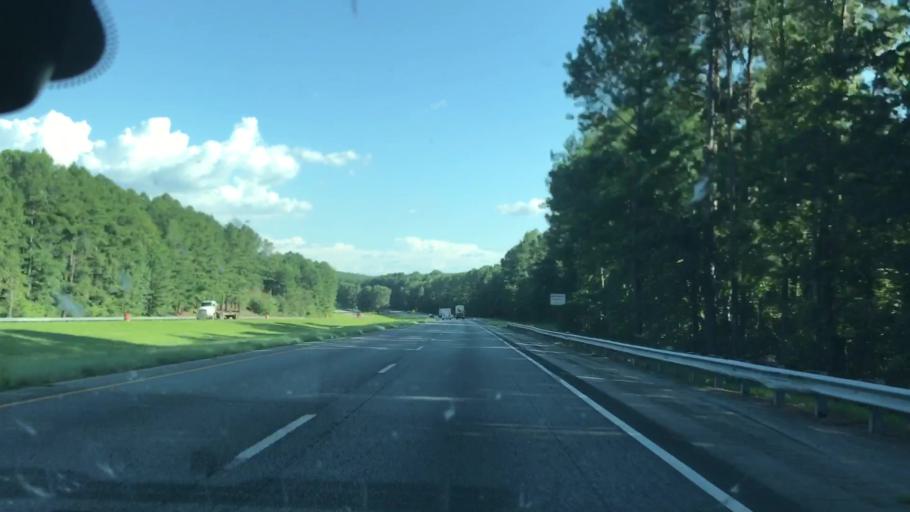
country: US
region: Georgia
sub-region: Harris County
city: Hamilton
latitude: 32.6428
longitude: -84.9705
